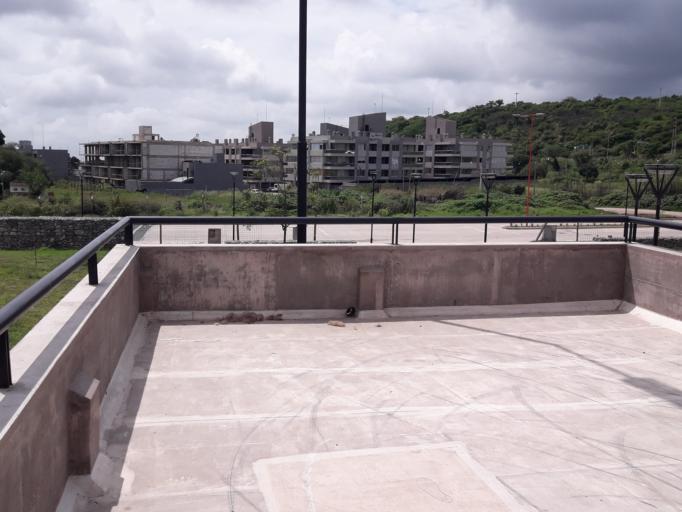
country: AR
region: Jujuy
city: San Salvador de Jujuy
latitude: -24.1830
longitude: -65.3291
